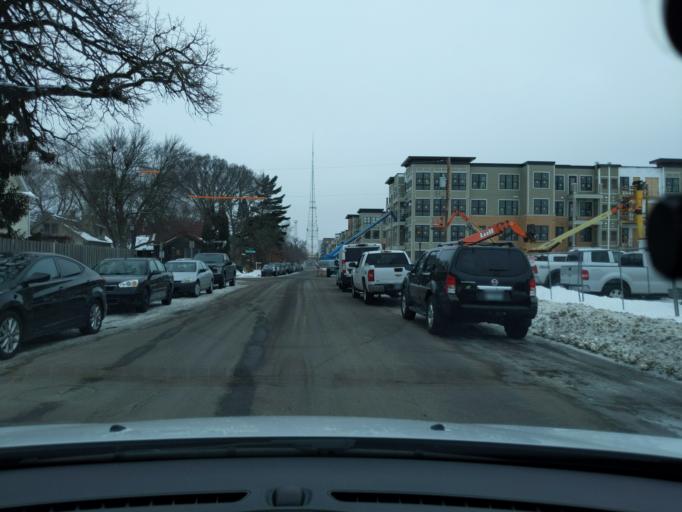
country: US
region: Minnesota
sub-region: Ramsey County
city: Lauderdale
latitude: 44.9623
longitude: -93.2077
